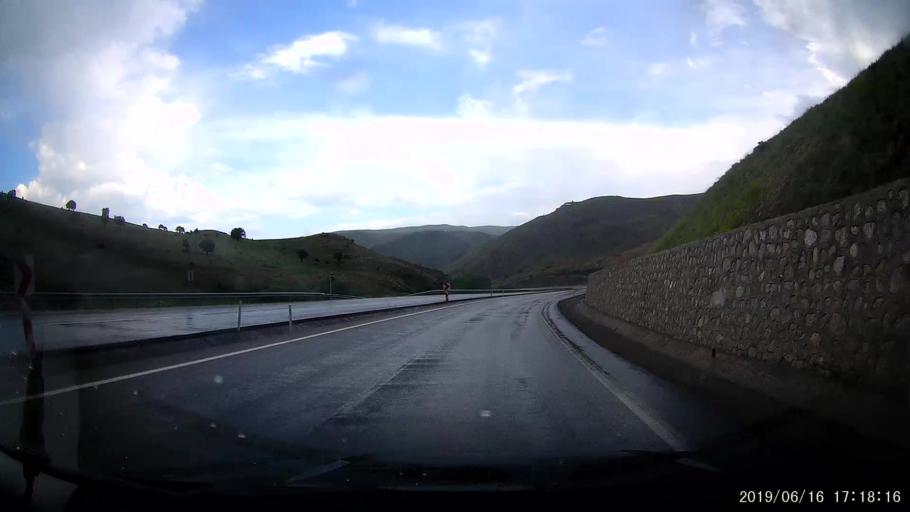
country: TR
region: Erzincan
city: Tercan
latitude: 39.8165
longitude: 40.5294
